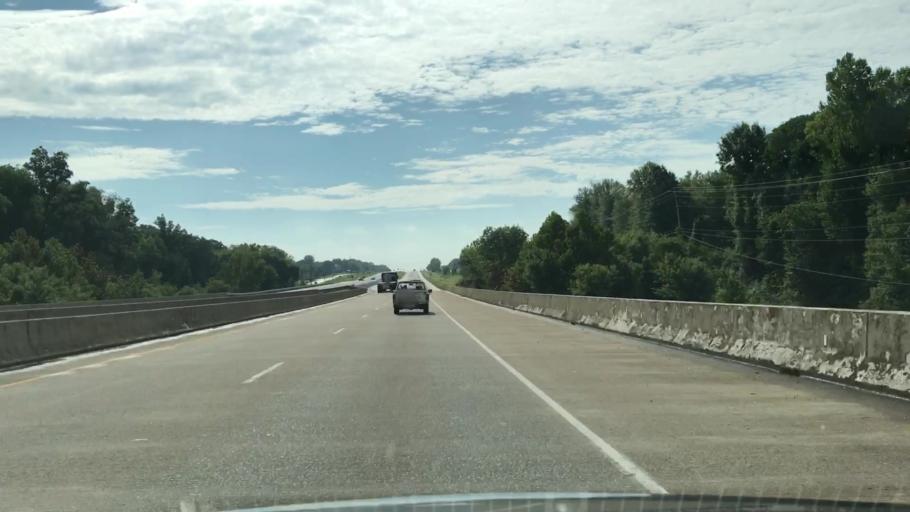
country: US
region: Kentucky
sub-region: Warren County
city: Plano
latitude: 36.8960
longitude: -86.3811
